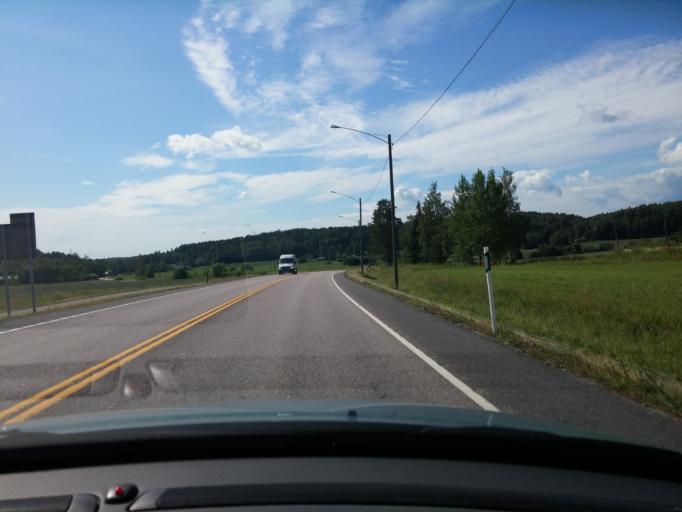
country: FI
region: Uusimaa
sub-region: Porvoo
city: Askola
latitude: 60.4475
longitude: 25.5857
